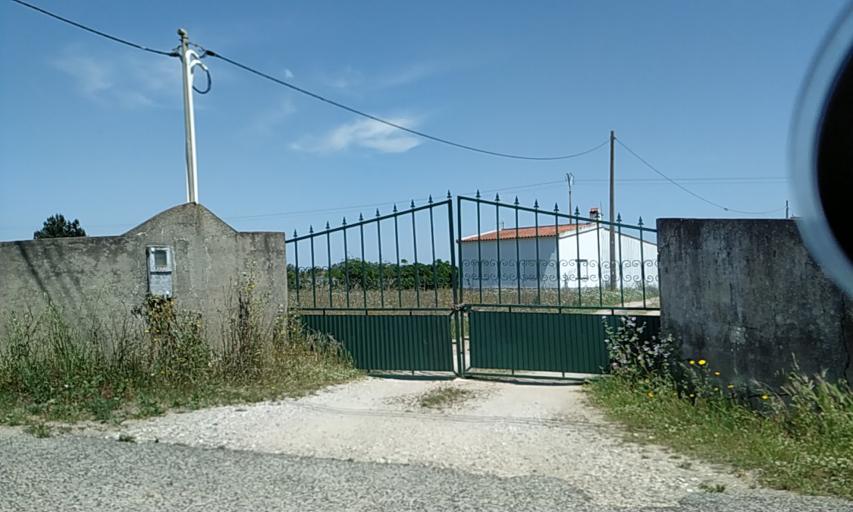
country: PT
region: Setubal
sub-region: Palmela
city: Pinhal Novo
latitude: 38.6415
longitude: -8.7429
